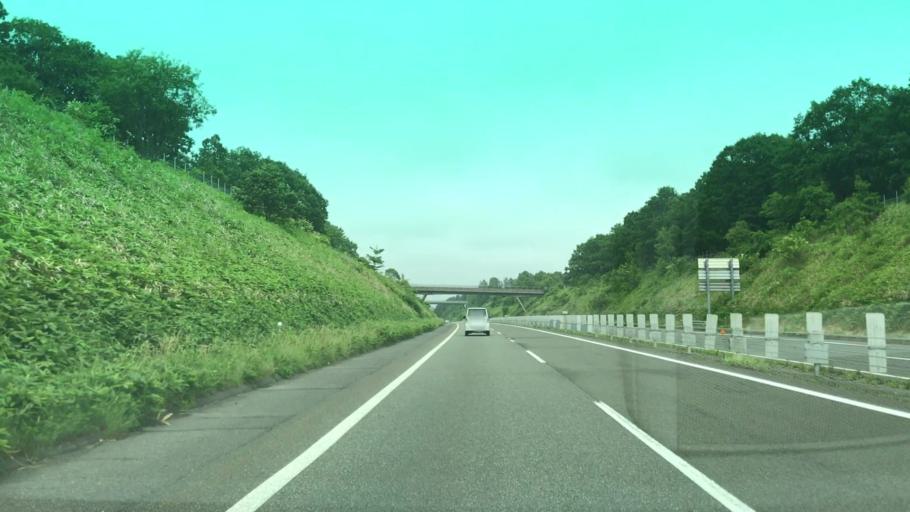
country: JP
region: Hokkaido
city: Tomakomai
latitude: 42.6196
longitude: 141.4758
